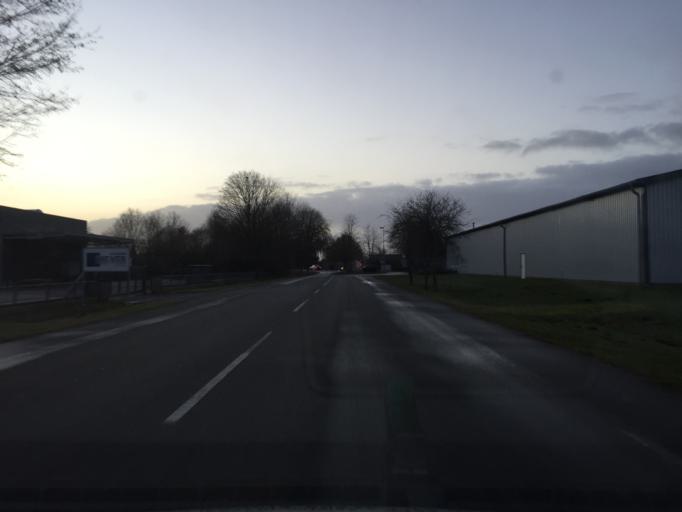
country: DE
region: Lower Saxony
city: Hassel
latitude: 52.6843
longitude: 8.8405
